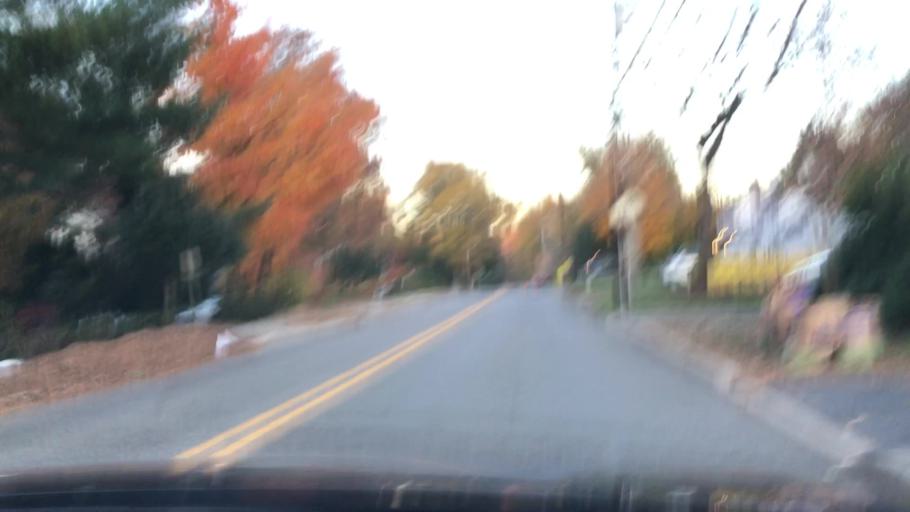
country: US
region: New Jersey
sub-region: Bergen County
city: Tenafly
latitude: 40.9248
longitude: -73.9733
